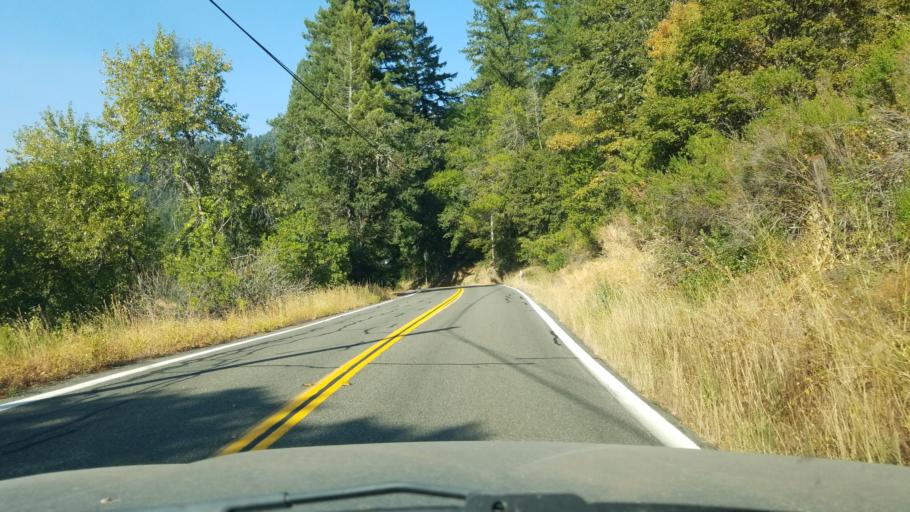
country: US
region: California
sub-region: Humboldt County
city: Redway
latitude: 40.1877
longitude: -123.7705
